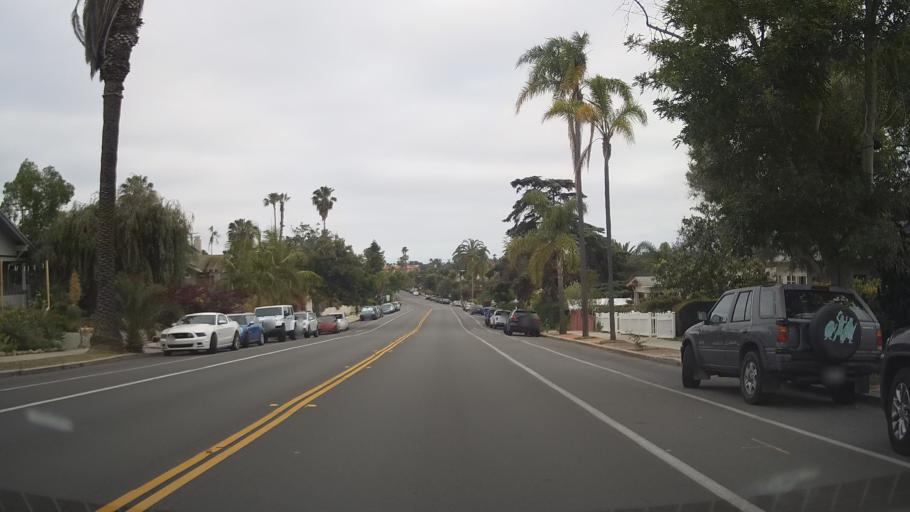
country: US
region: California
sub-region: San Diego County
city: San Diego
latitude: 32.7569
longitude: -117.1513
